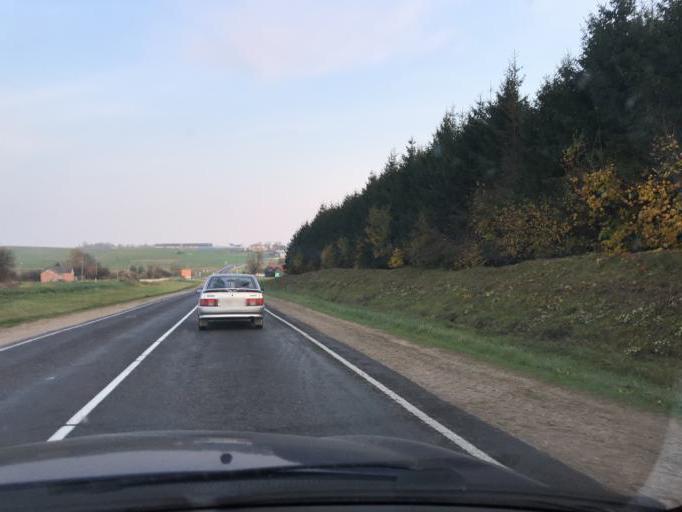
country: BY
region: Grodnenskaya
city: Karelichy
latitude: 53.5901
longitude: 26.0953
